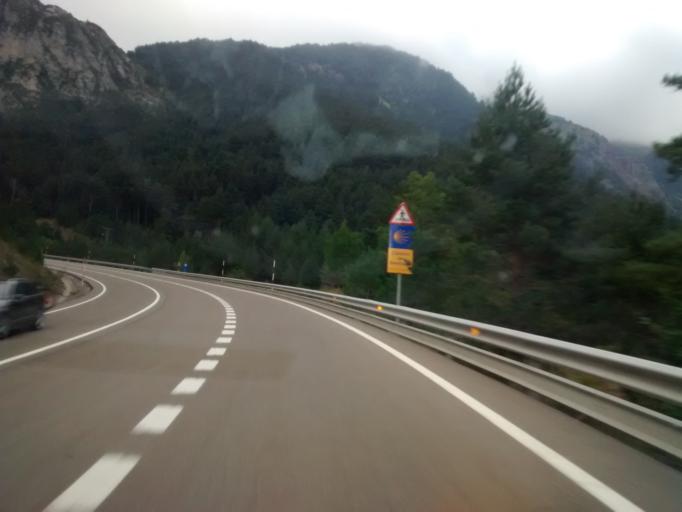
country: ES
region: Aragon
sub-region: Provincia de Huesca
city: Canfranc
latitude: 42.7736
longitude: -0.5087
